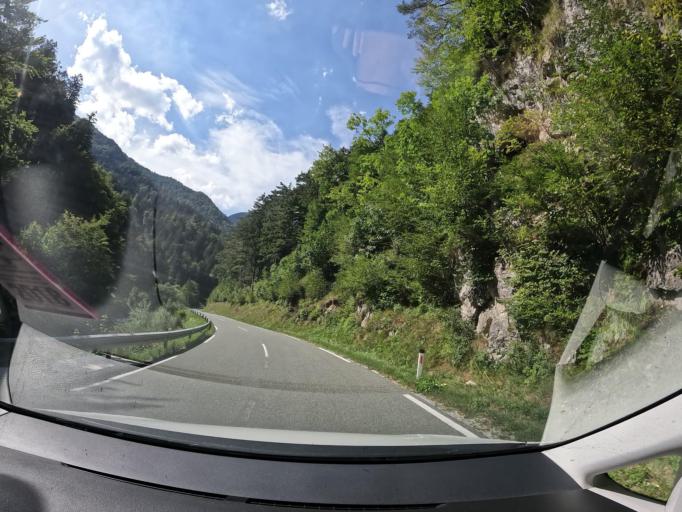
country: SI
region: Jezersko
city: Zgornje Jezersko
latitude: 46.3635
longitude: 14.4530
